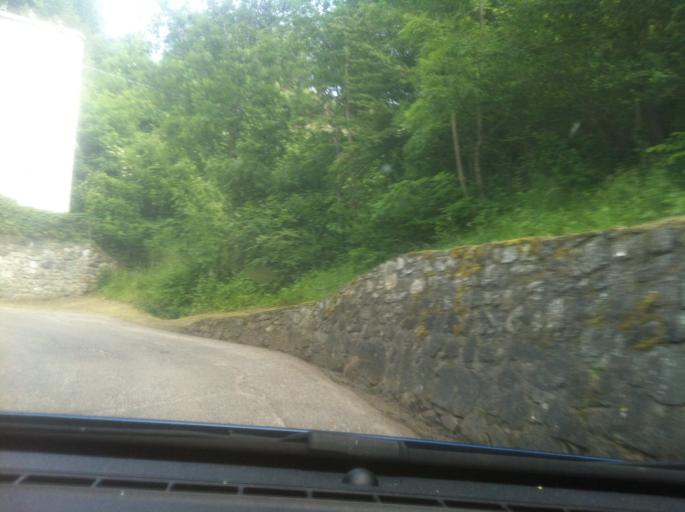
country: IT
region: Aosta Valley
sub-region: Valle d'Aosta
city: Saint Marcel
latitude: 45.7229
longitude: 7.4615
